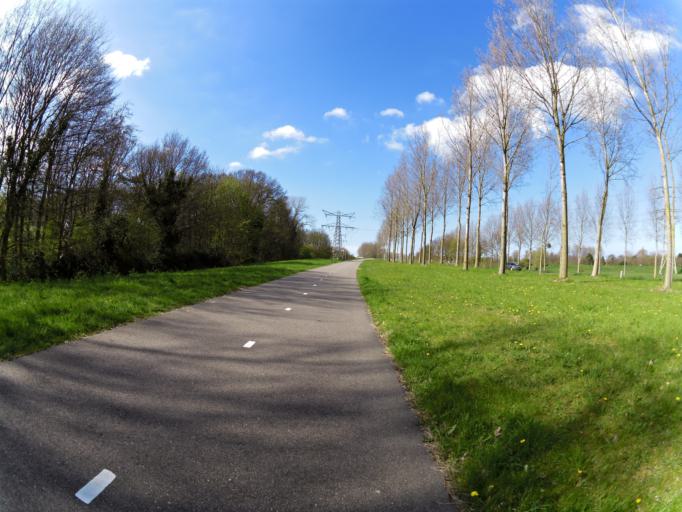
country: NL
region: South Holland
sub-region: Gemeente Brielle
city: Brielle
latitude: 51.9193
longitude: 4.1061
